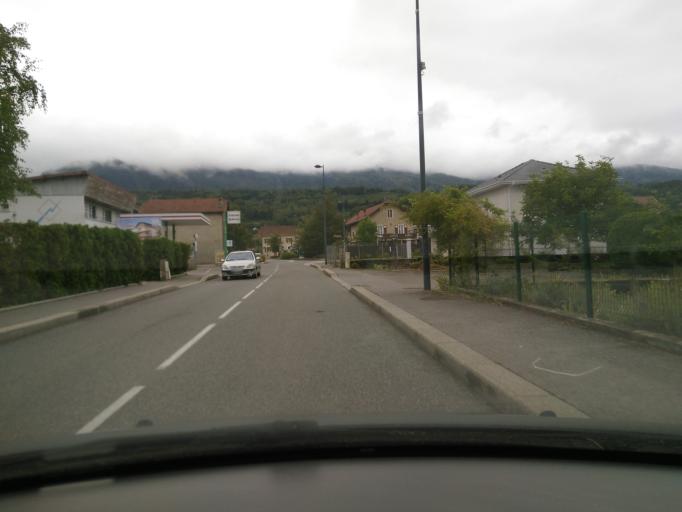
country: FR
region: Rhone-Alpes
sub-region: Departement de la Haute-Savoie
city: Amancy
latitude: 46.0626
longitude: 6.3638
